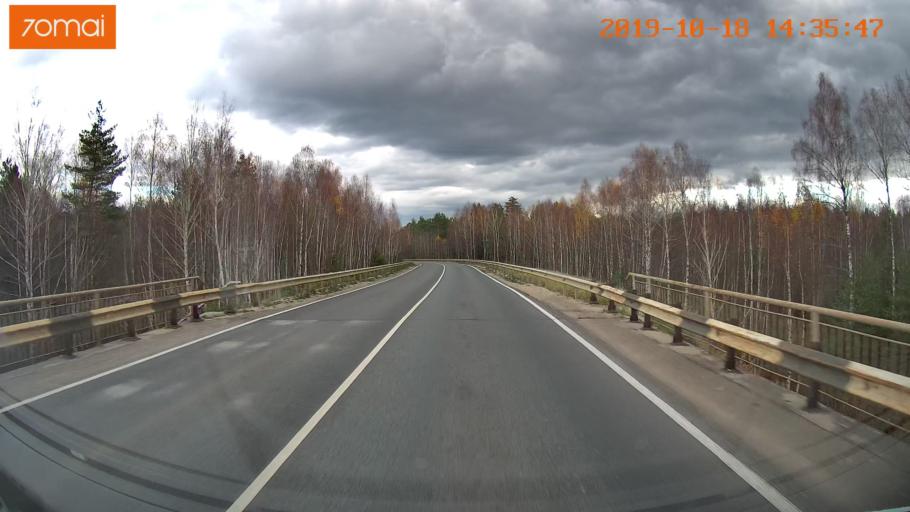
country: RU
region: Vladimir
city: Velikodvorskiy
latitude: 55.2218
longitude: 40.6455
